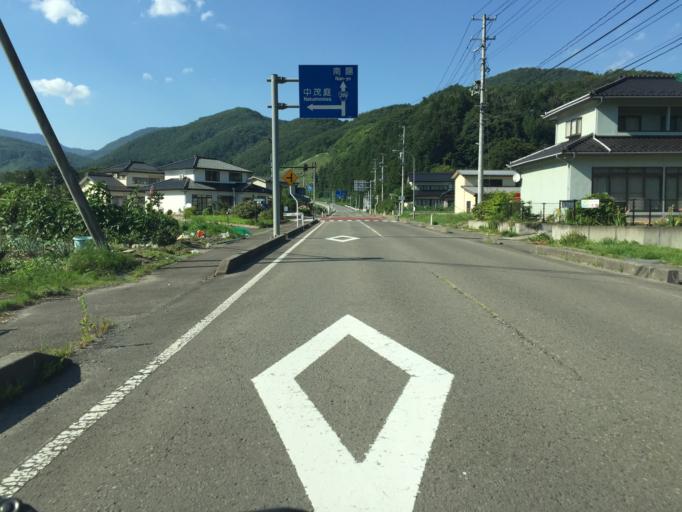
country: JP
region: Fukushima
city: Hobaramachi
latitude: 37.9134
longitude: 140.4269
